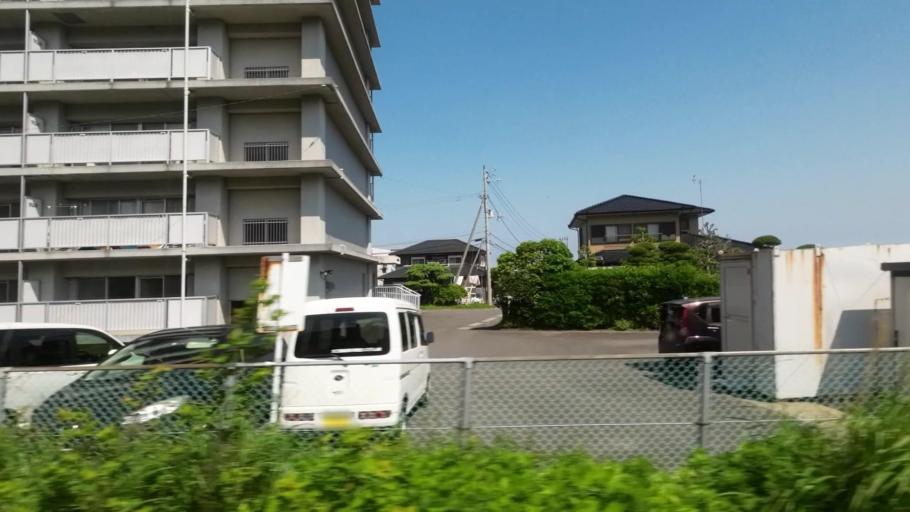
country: JP
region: Ehime
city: Kawanoecho
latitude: 33.9715
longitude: 133.5207
